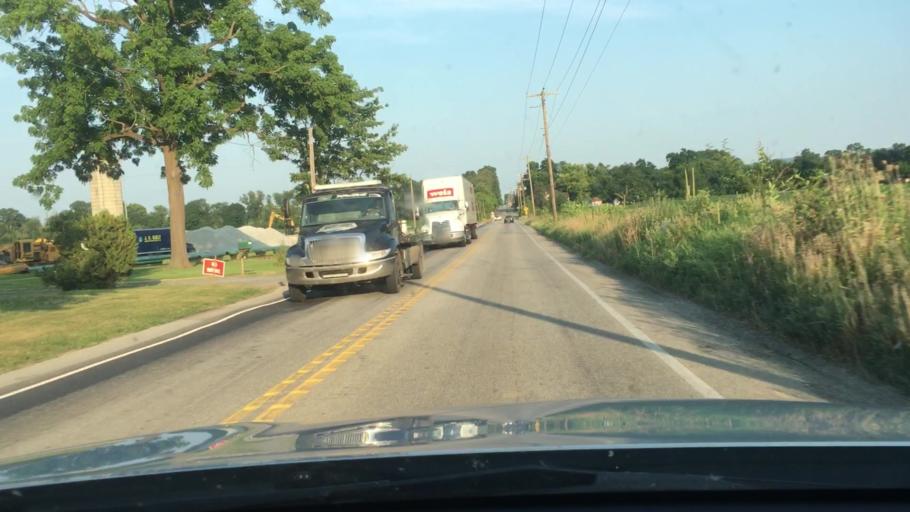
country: US
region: Pennsylvania
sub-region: Cumberland County
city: Boiling Springs
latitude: 40.1803
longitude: -77.1365
